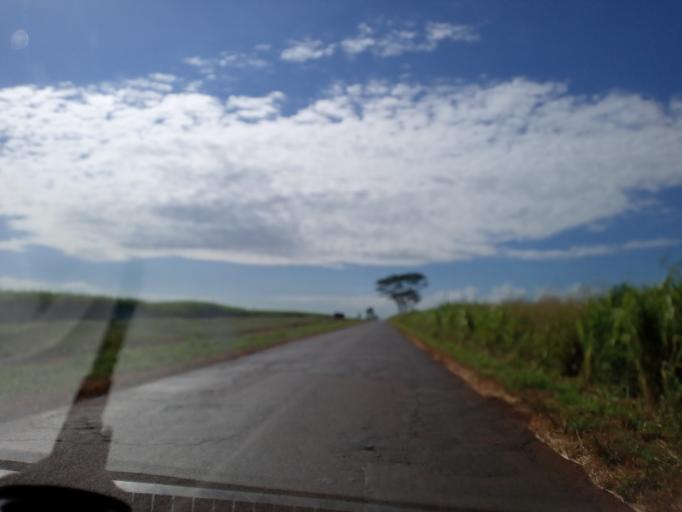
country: BR
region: Goias
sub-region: Itumbiara
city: Itumbiara
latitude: -18.4516
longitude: -49.1588
